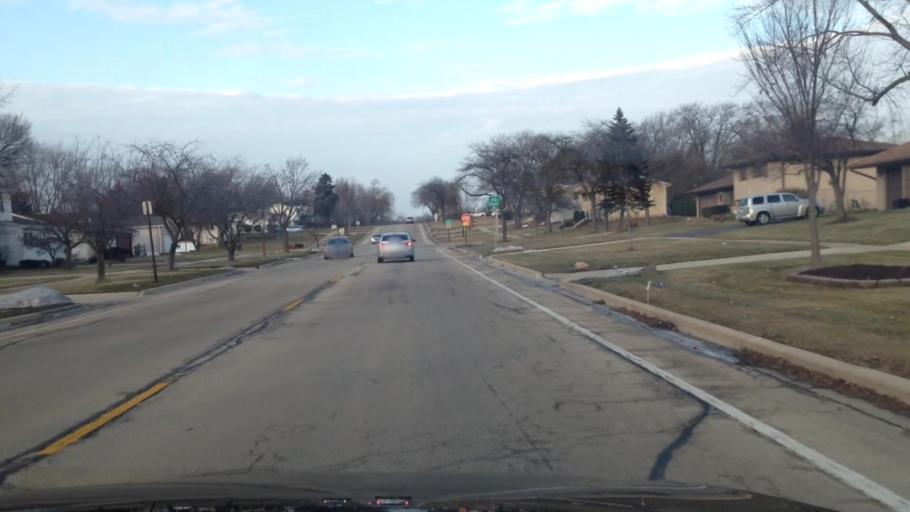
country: US
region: Illinois
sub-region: Cook County
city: Schaumburg
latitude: 42.0122
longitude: -88.0996
